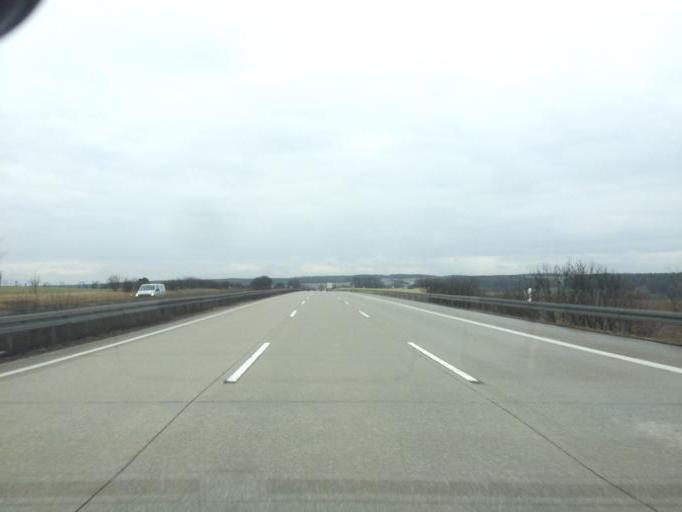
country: DE
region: Thuringia
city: Eineborn
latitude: 50.8374
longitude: 11.8701
